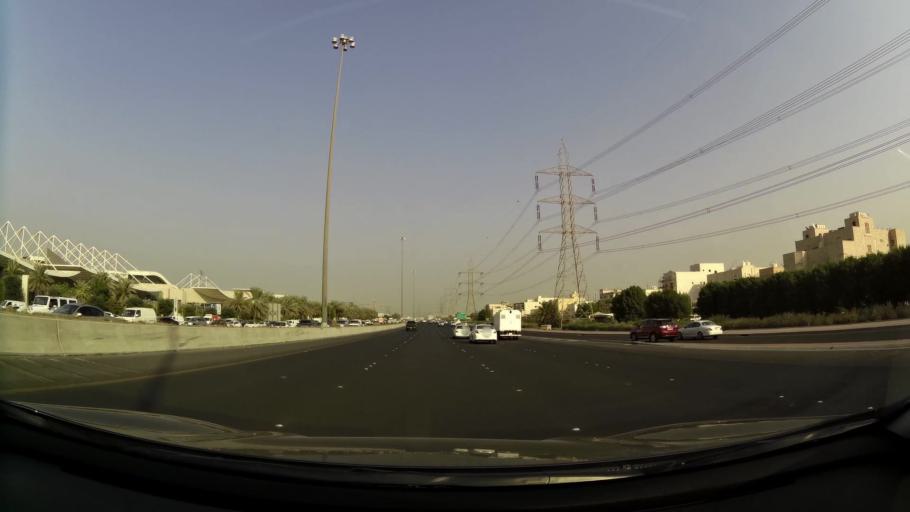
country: KW
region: Al Asimah
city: Ar Rabiyah
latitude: 29.3007
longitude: 47.9312
